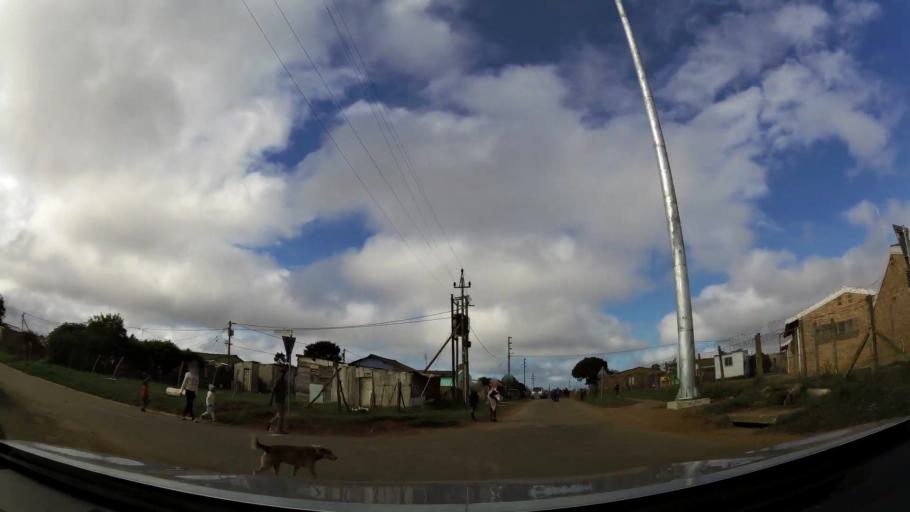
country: ZA
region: Western Cape
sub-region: Eden District Municipality
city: Plettenberg Bay
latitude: -34.0477
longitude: 23.3239
